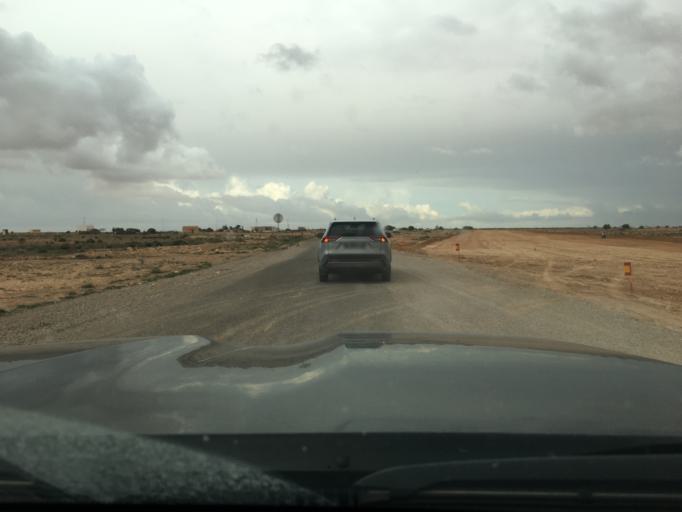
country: TN
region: Madanin
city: Medenine
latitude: 33.3020
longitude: 10.6105
